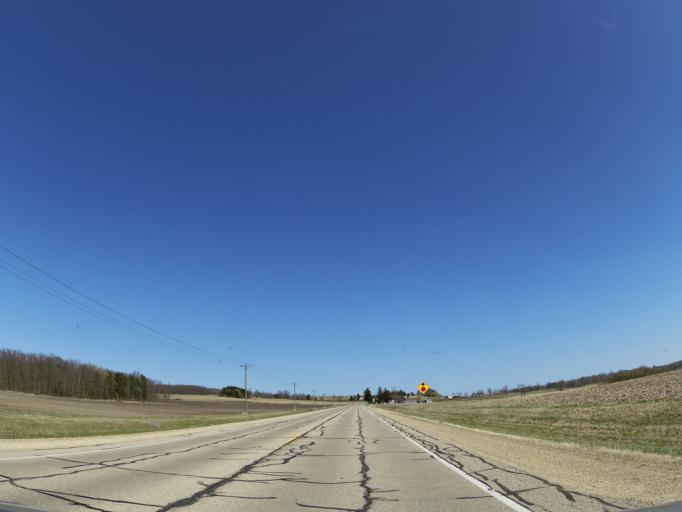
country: US
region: Wisconsin
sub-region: Saint Croix County
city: Baldwin
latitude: 44.8478
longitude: -92.3819
